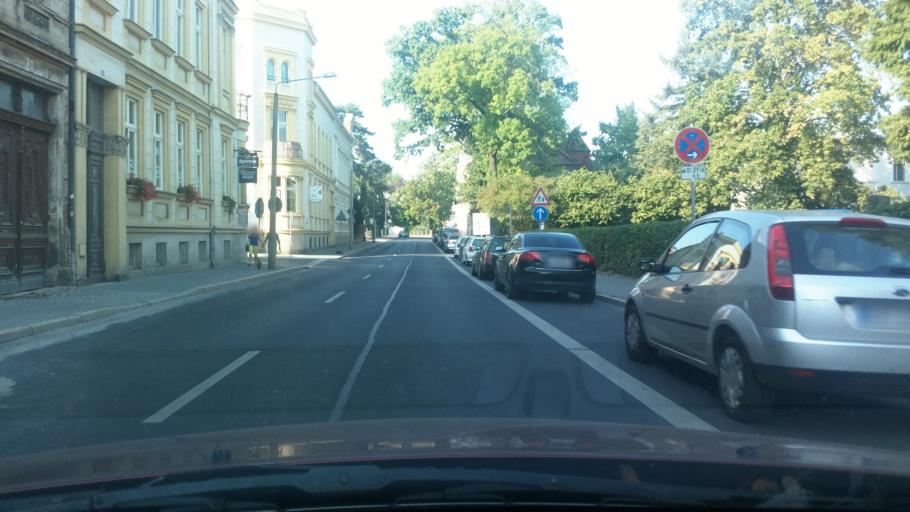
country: DE
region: Saxony
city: Goerlitz
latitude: 51.1487
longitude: 14.9906
